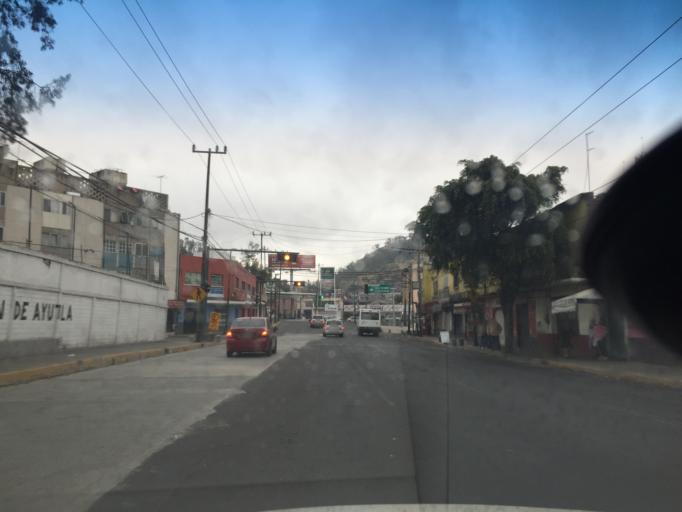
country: MX
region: Mexico City
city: Gustavo A. Madero
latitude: 19.4865
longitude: -99.1131
